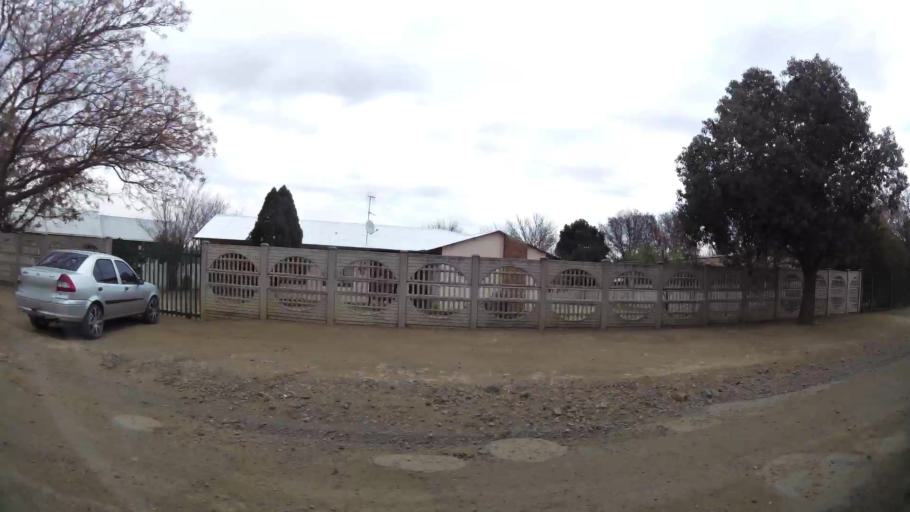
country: ZA
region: Orange Free State
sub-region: Fezile Dabi District Municipality
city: Kroonstad
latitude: -27.6834
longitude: 27.2288
